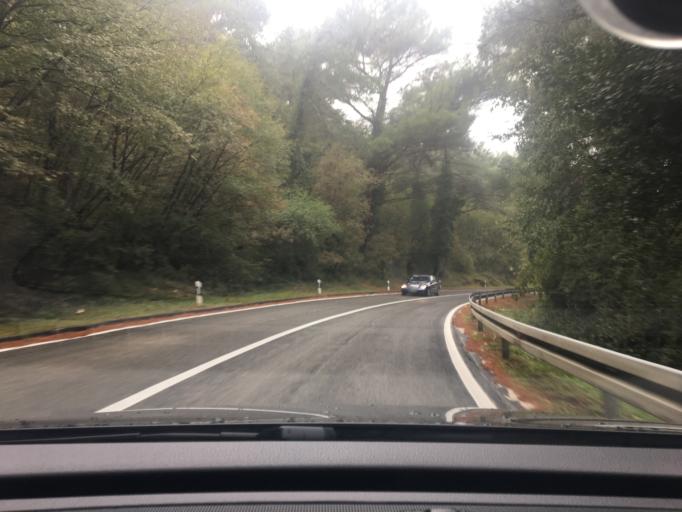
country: HR
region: Istarska
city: Buje
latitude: 45.4489
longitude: 13.6522
